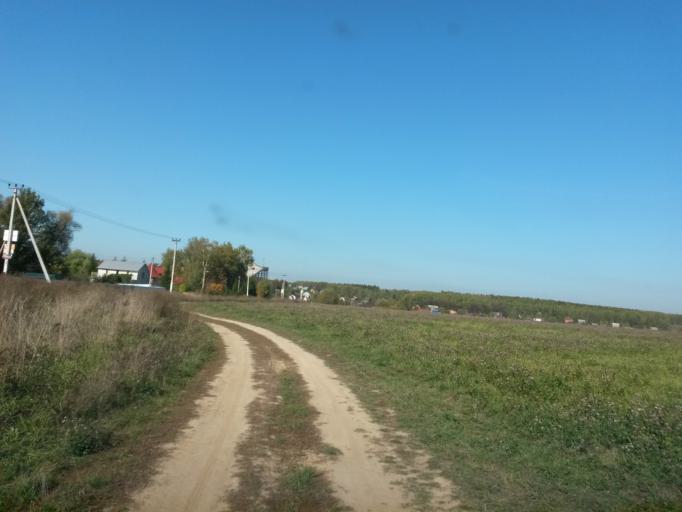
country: RU
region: Moskovskaya
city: Lyubuchany
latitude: 55.2597
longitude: 37.6105
